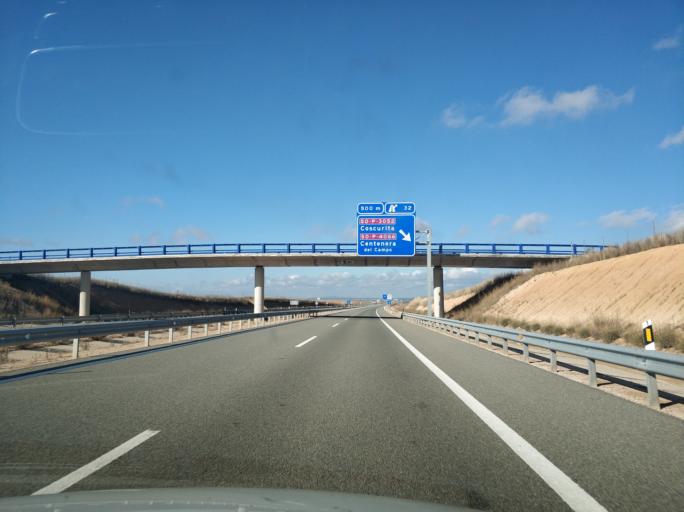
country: ES
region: Castille and Leon
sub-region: Provincia de Soria
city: Coscurita
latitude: 41.4107
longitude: -2.4840
